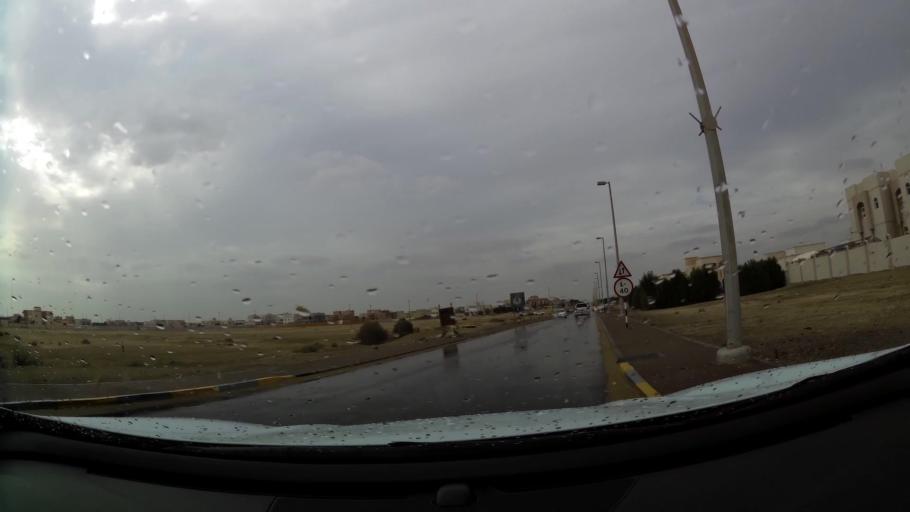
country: AE
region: Abu Dhabi
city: Abu Dhabi
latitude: 24.3568
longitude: 54.6275
